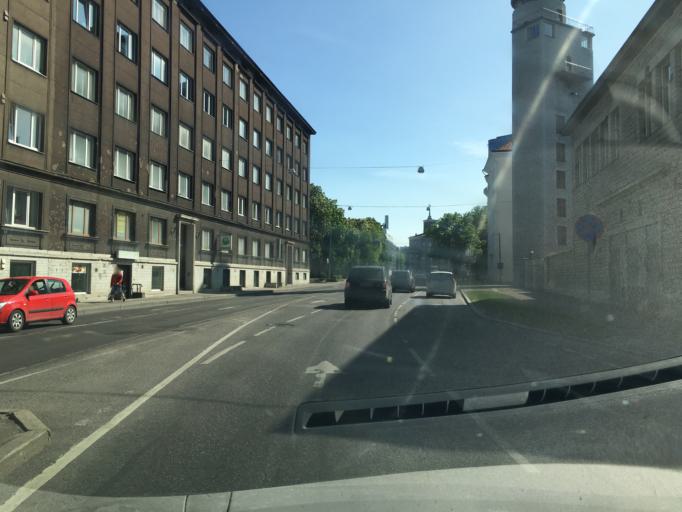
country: EE
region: Harju
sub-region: Tallinna linn
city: Tallinn
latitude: 59.4355
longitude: 24.7648
